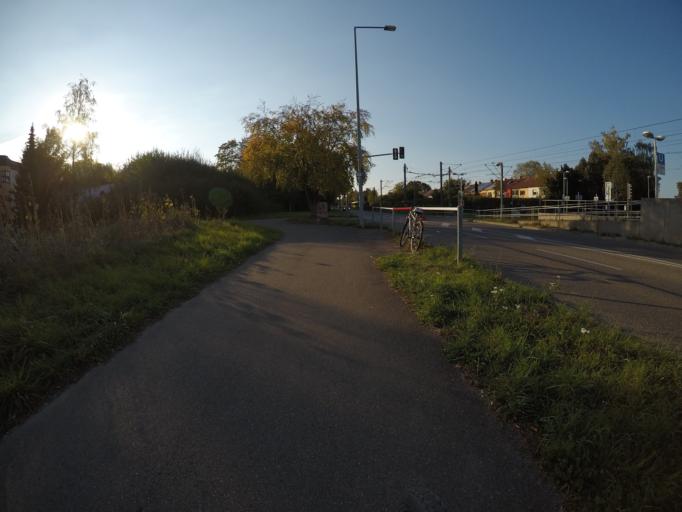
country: DE
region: Baden-Wuerttemberg
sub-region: Regierungsbezirk Stuttgart
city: Ostfildern
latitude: 48.7380
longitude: 9.2334
